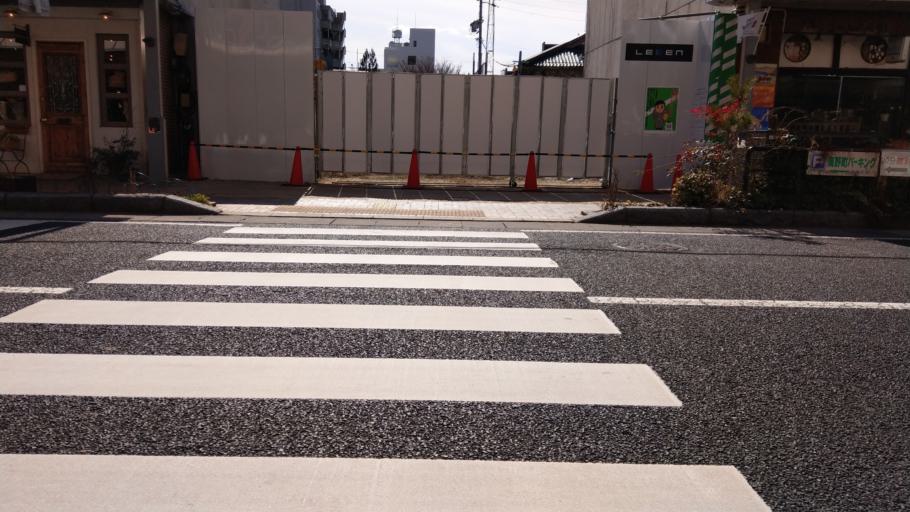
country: JP
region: Nagano
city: Ueda
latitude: 36.4000
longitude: 138.2544
